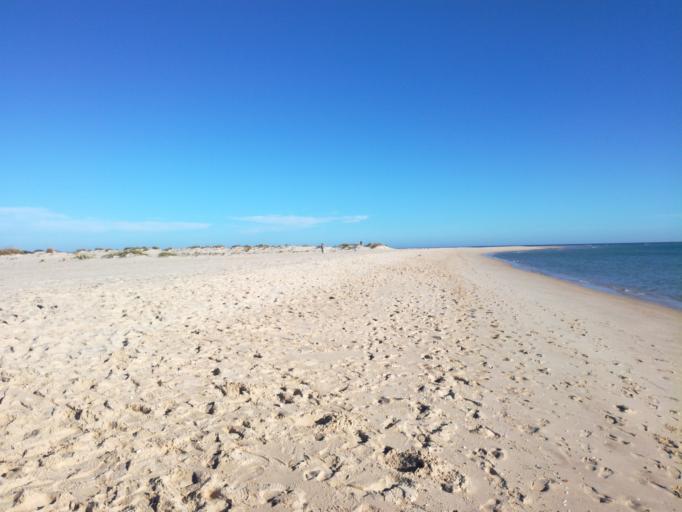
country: PT
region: Faro
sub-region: Olhao
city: Olhao
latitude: 37.0124
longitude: -7.7957
